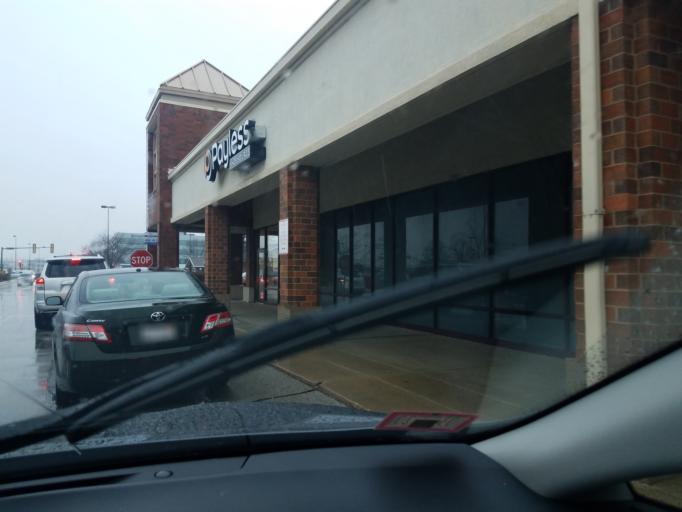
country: US
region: Illinois
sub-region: Cook County
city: Morton Grove
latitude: 42.0106
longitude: -87.7676
